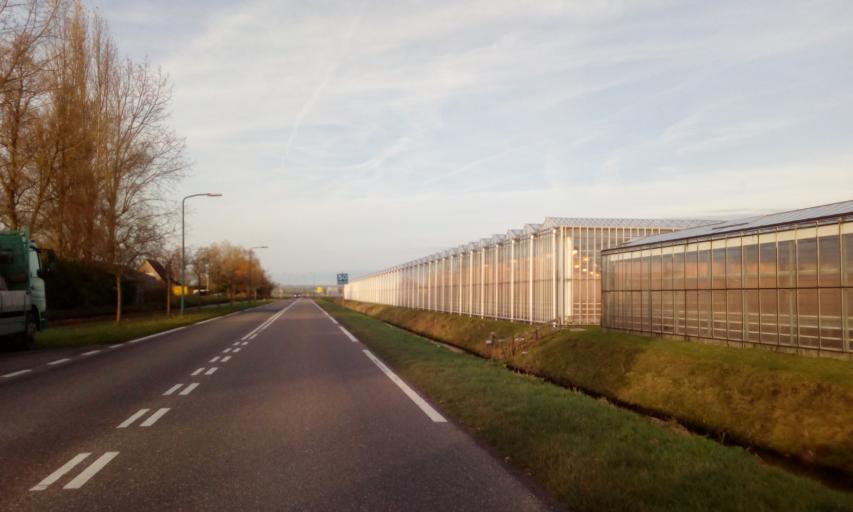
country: NL
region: South Holland
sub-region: Gemeente Lansingerland
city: Bleiswijk
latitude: 52.0247
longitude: 4.5076
